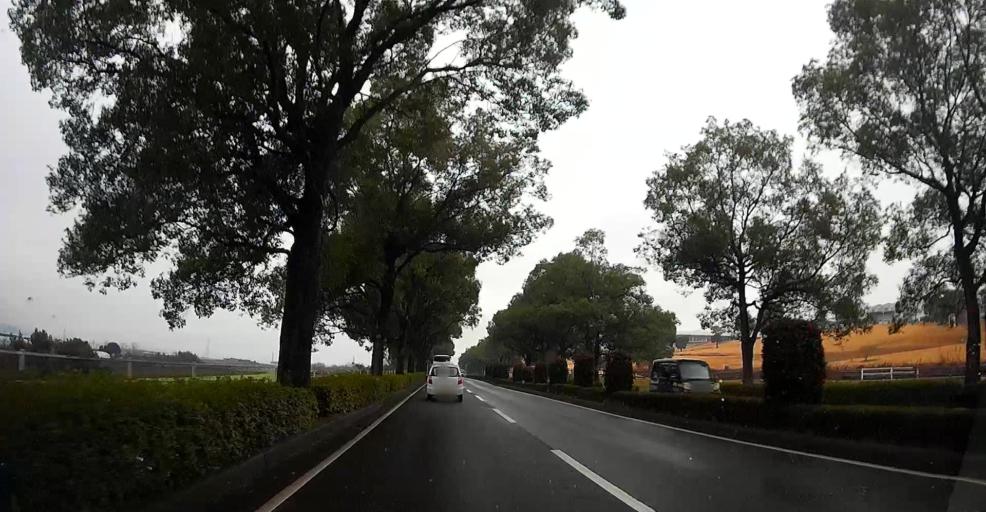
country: JP
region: Kumamoto
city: Ozu
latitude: 32.8147
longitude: 130.8358
